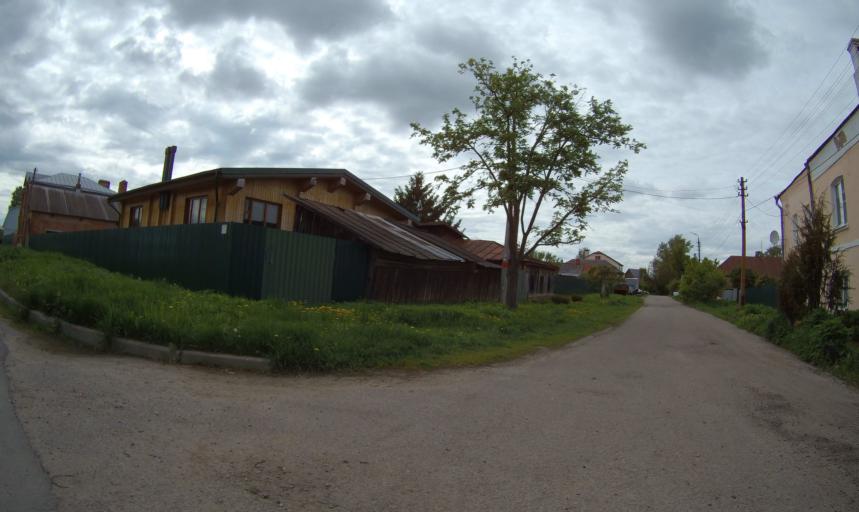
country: RU
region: Moskovskaya
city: Kolomna
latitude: 55.1005
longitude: 38.7461
